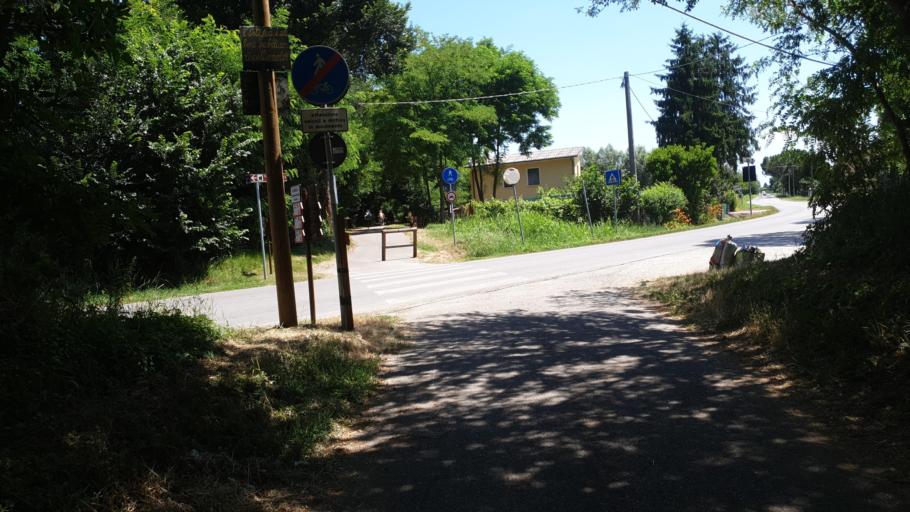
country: IT
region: Veneto
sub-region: Provincia di Padova
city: San Giorgio delle Pertiche
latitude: 45.5490
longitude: 11.8660
